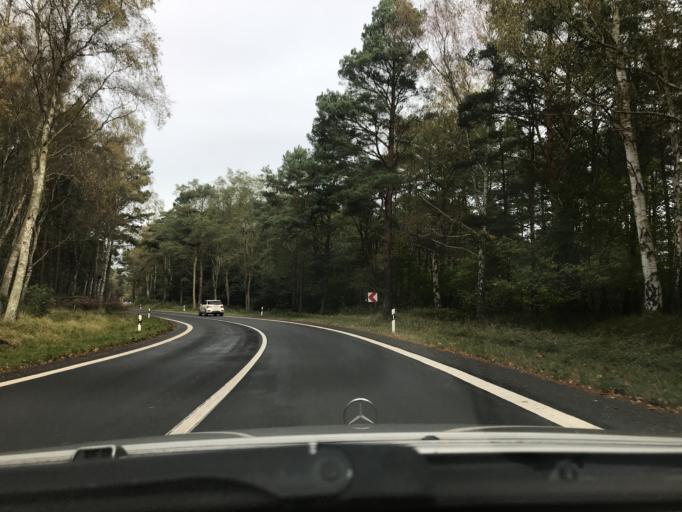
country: DE
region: Mecklenburg-Vorpommern
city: Karlshagen
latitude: 54.1318
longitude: 13.8306
